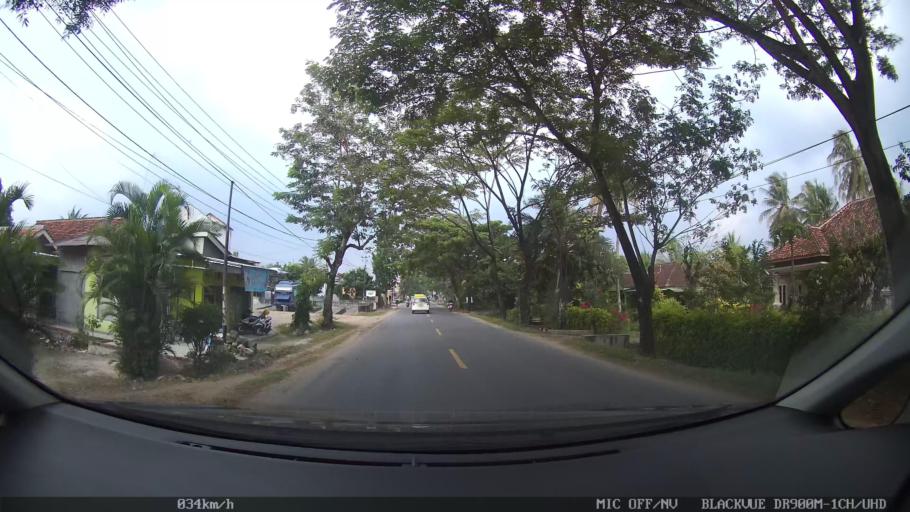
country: ID
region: Lampung
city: Gadingrejo
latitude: -5.3732
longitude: 105.0442
